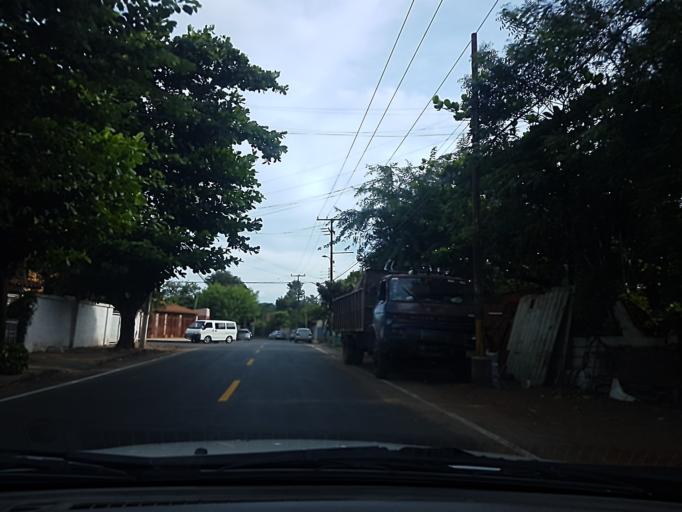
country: PY
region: Central
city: San Lorenzo
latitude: -25.2684
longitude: -57.4750
